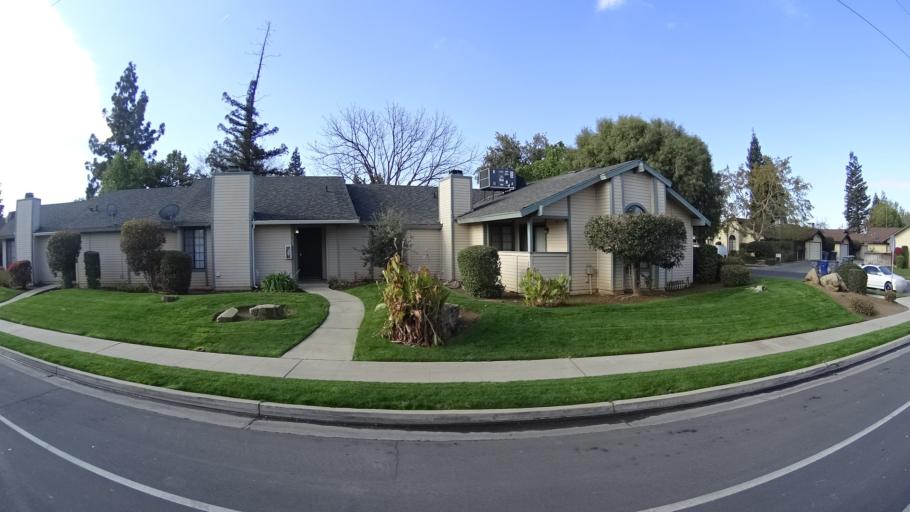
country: US
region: California
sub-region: Fresno County
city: West Park
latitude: 36.8051
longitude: -119.8526
